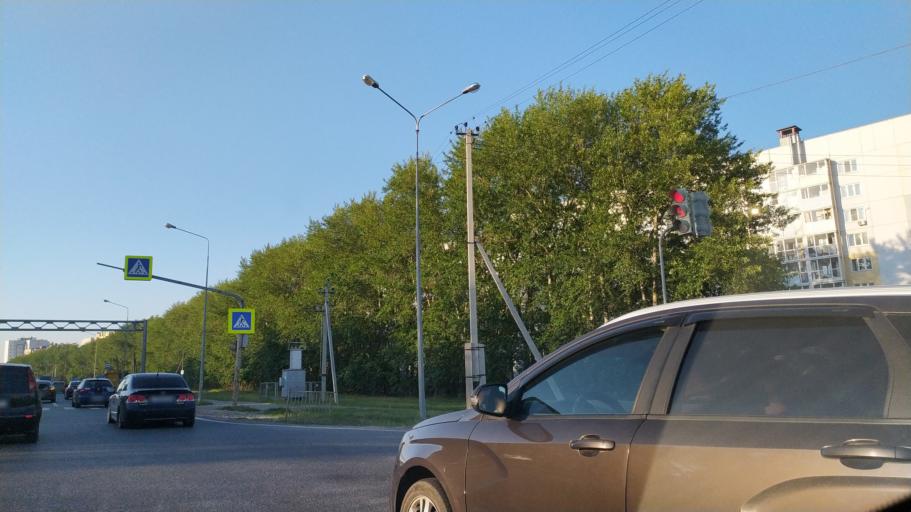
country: RU
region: Chuvashia
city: Kugesi
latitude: 56.0656
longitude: 47.2791
